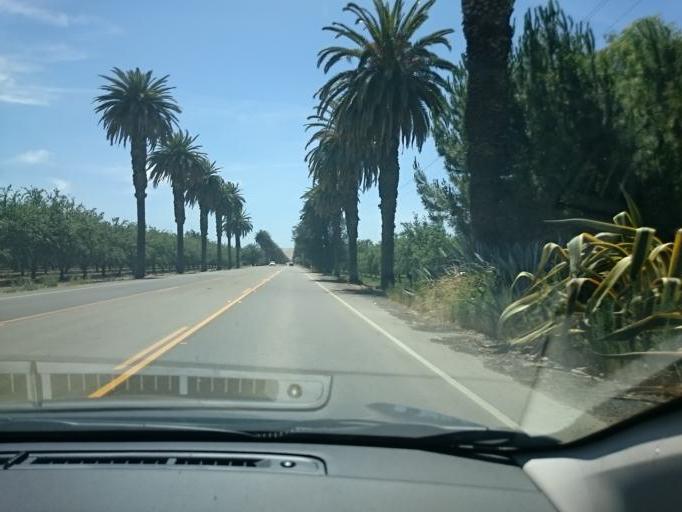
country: US
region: California
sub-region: Stanislaus County
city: Patterson
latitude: 37.4862
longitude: -121.0983
